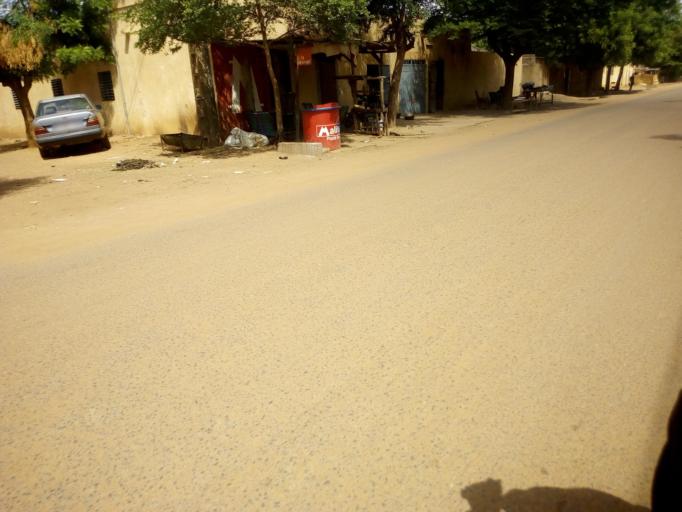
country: ML
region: Segou
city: Segou
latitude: 13.4334
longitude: -6.2639
